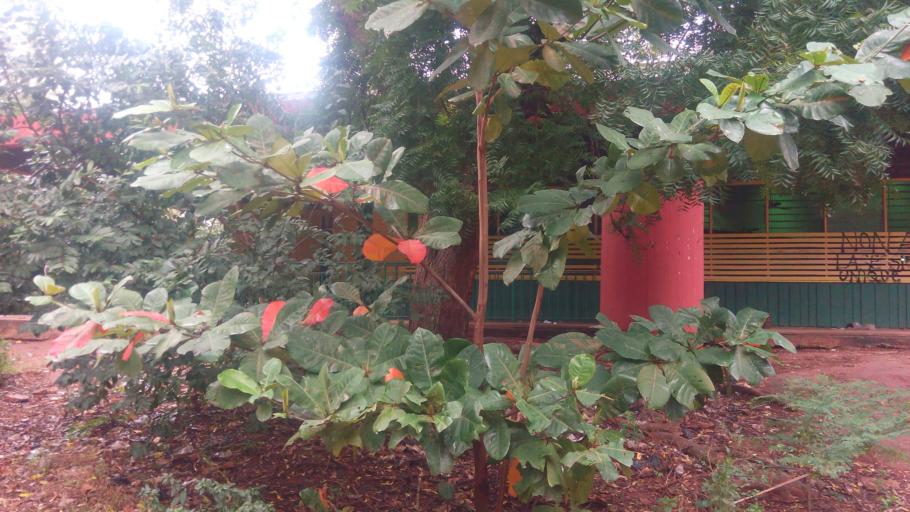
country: BJ
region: Atlantique
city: Abomey-Calavi
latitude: 6.4141
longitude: 2.3431
